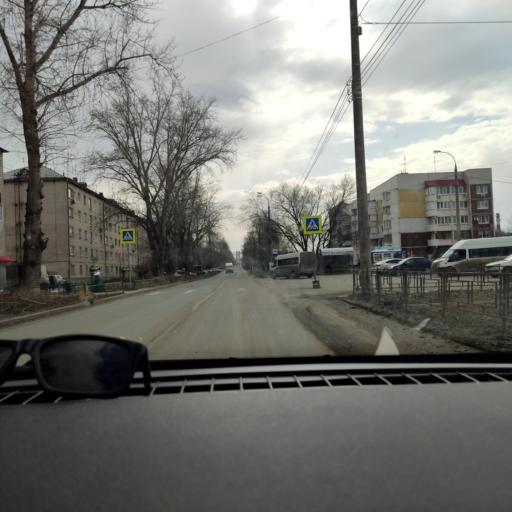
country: RU
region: Samara
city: Bereza
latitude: 53.5162
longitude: 50.1401
